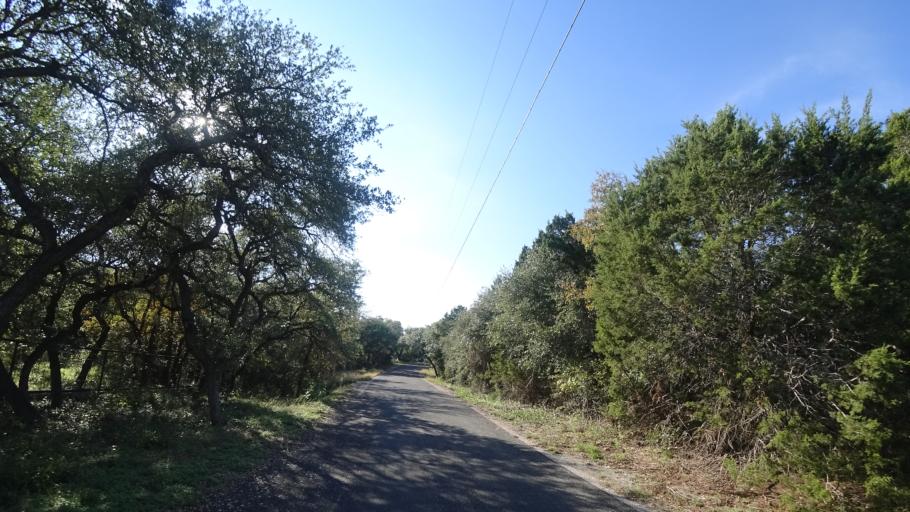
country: US
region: Texas
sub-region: Travis County
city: Bee Cave
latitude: 30.2380
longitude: -97.9257
